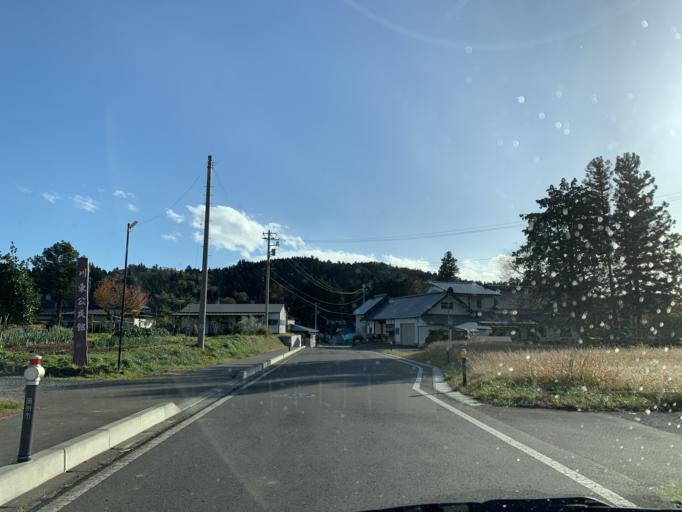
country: JP
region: Iwate
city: Ichinoseki
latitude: 39.0095
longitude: 141.0968
